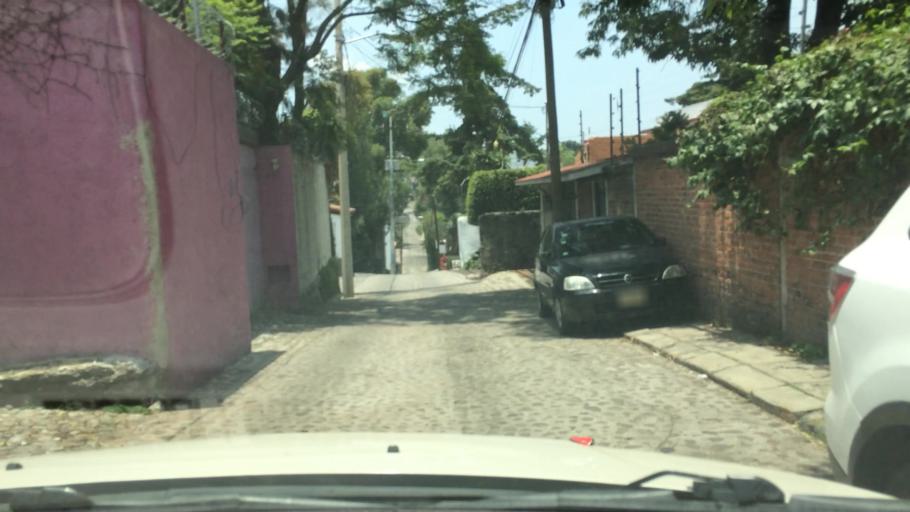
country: MX
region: Mexico City
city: Magdalena Contreras
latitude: 19.3248
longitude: -99.2262
